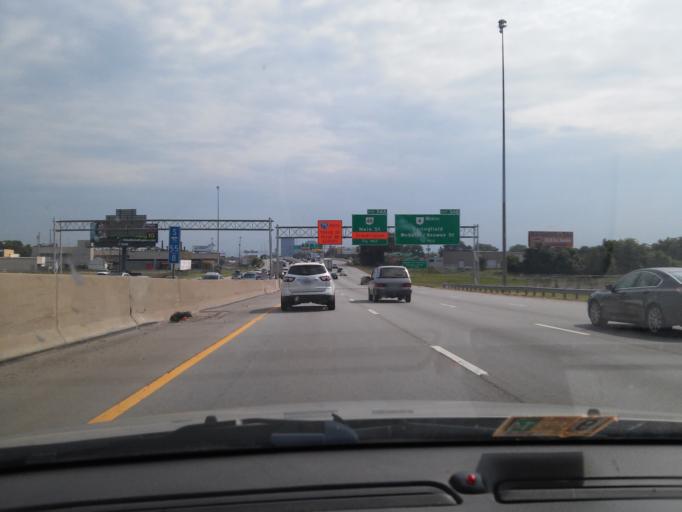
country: US
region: Ohio
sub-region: Montgomery County
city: Northridge
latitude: 39.7869
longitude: -84.1841
